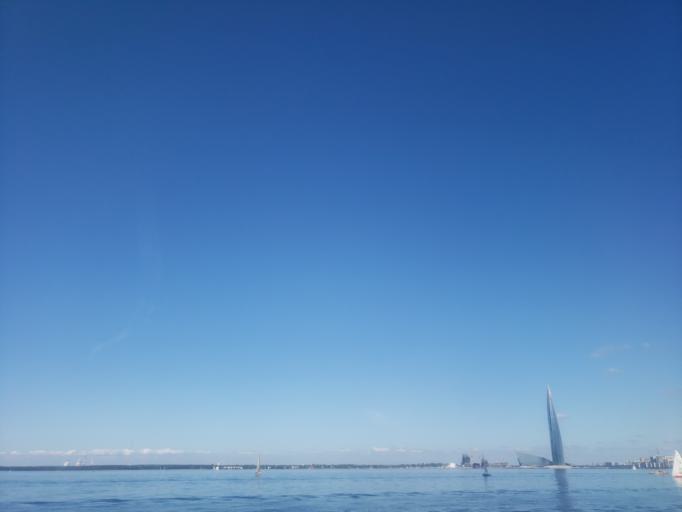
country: RU
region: St.-Petersburg
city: Lakhtinskiy
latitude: 59.9565
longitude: 30.1624
